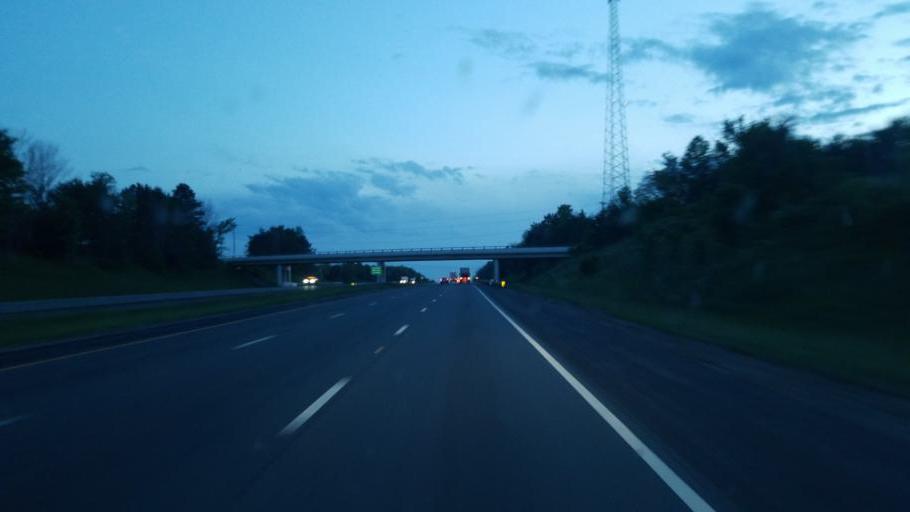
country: US
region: Ohio
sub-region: Richland County
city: Lexington
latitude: 40.5688
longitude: -82.6223
